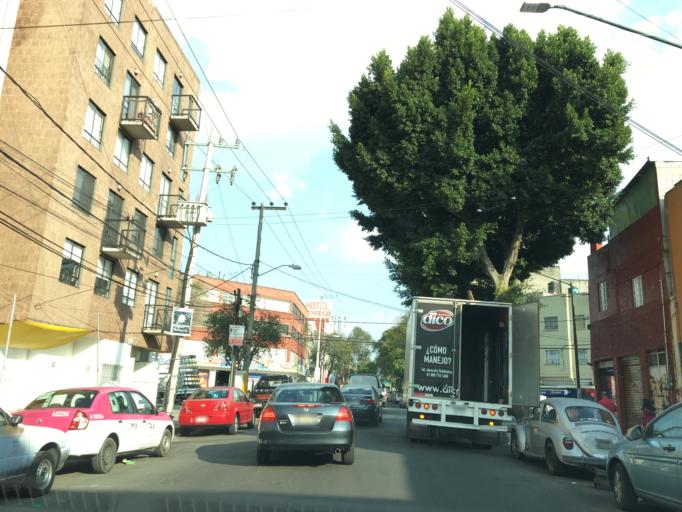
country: MX
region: Mexico City
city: Mexico City
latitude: 19.4180
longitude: -99.1466
